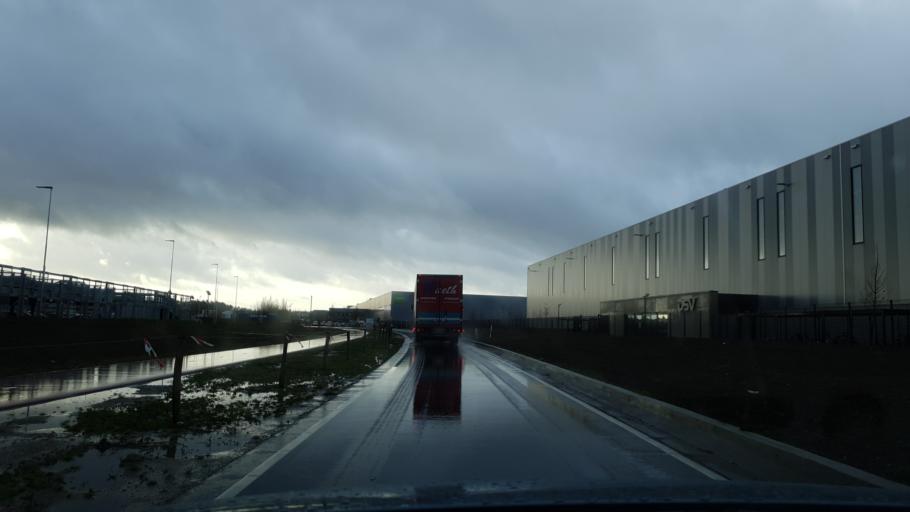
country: NL
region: Limburg
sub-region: Gemeente Peel en Maas
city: Maasbree
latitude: 51.4114
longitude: 6.0952
